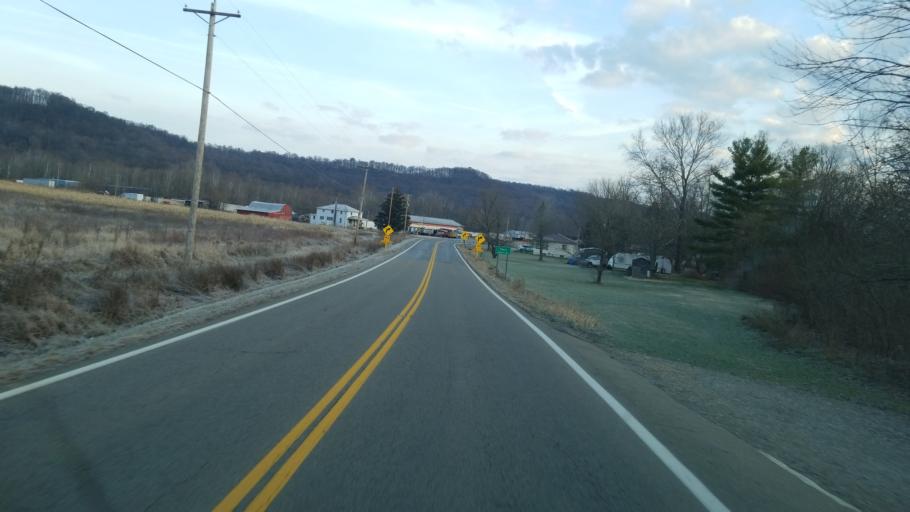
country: US
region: Ohio
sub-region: Ross County
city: Frankfort
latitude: 39.2505
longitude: -83.2038
